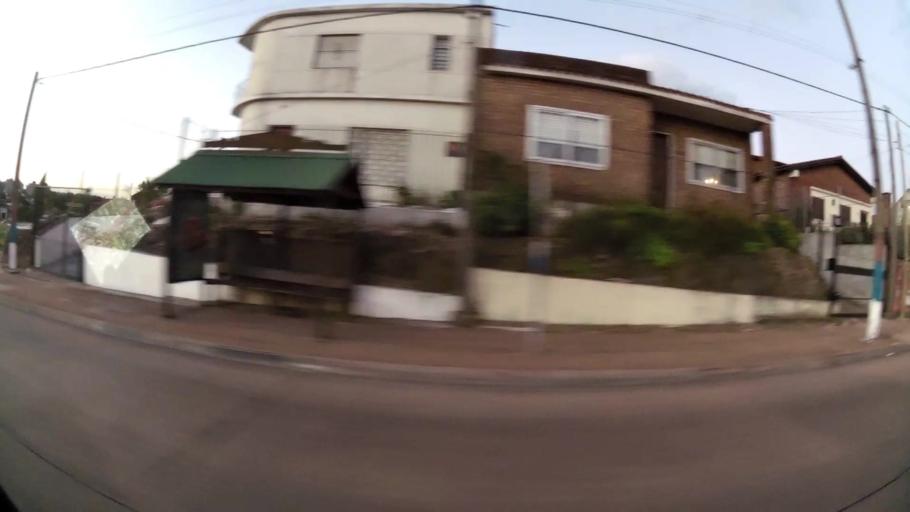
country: UY
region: Canelones
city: Paso de Carrasco
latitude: -34.8858
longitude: -56.1039
